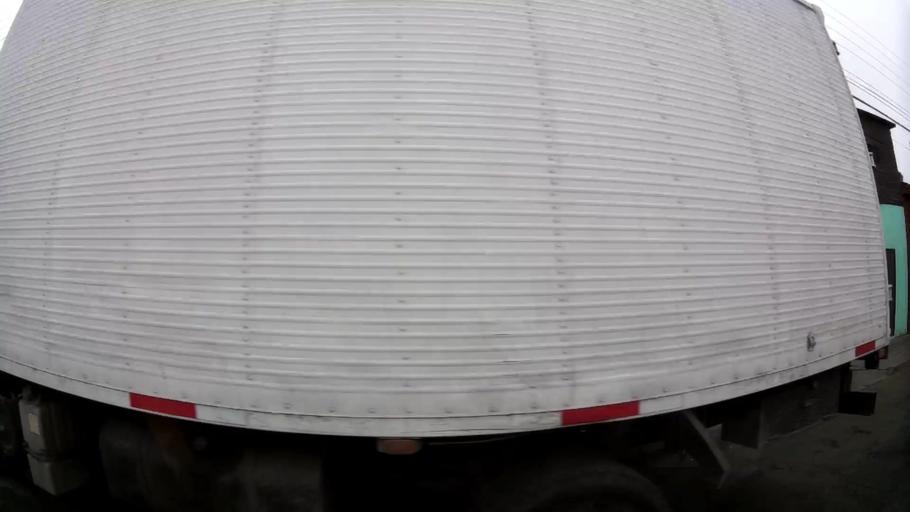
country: CL
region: Santiago Metropolitan
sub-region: Provincia de Santiago
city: Santiago
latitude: -33.4958
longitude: -70.6430
